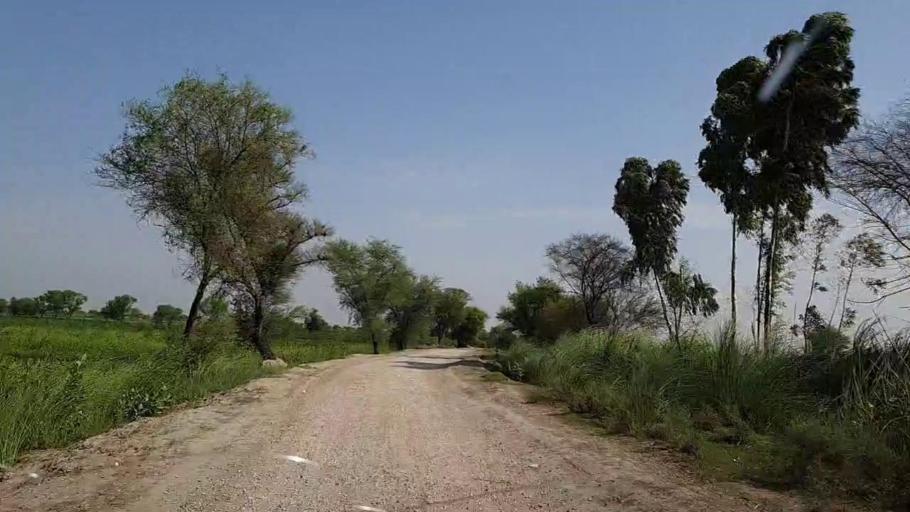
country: PK
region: Sindh
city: Khanpur
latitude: 27.7250
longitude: 69.3600
